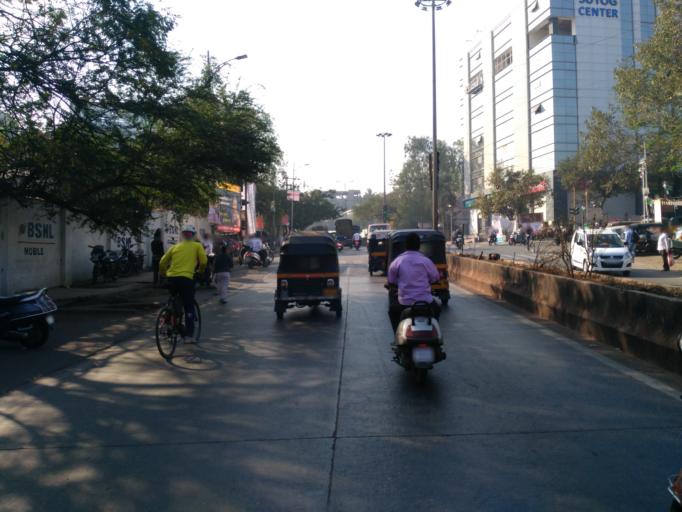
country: IN
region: Maharashtra
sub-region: Pune Division
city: Pune
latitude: 18.4934
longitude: 73.8693
